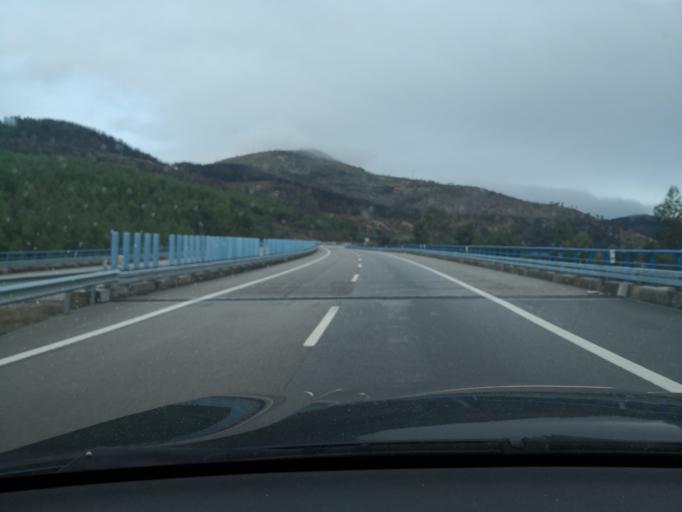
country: PT
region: Vila Real
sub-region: Ribeira de Pena
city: Ribeira de Pena
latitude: 41.4813
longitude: -7.8675
